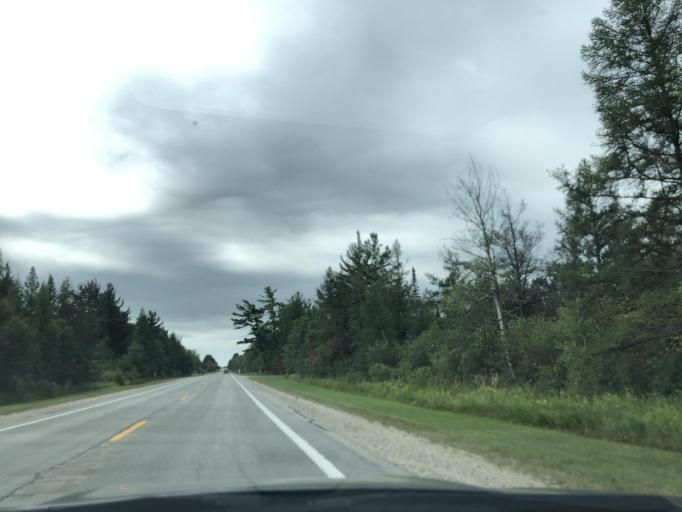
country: US
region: Michigan
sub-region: Missaukee County
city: Lake City
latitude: 44.2487
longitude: -85.2152
